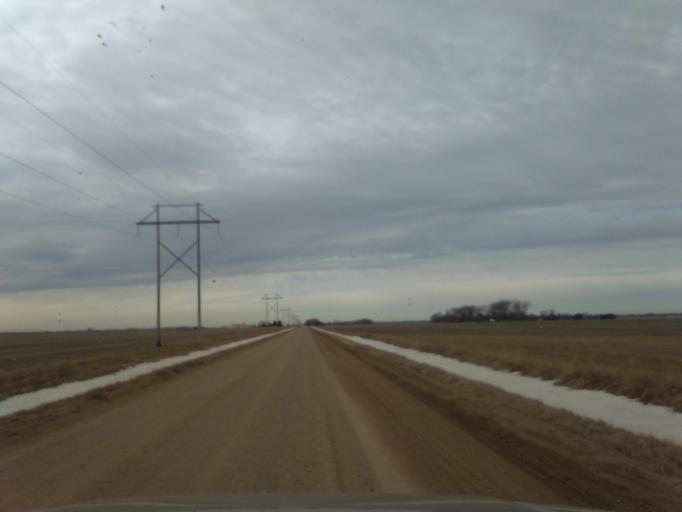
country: US
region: Nebraska
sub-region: Buffalo County
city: Gibbon
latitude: 40.6550
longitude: -98.7831
